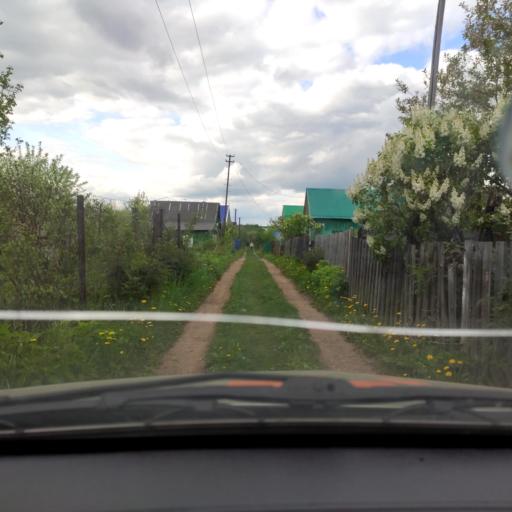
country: RU
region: Bashkortostan
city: Blagoveshchensk
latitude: 54.9413
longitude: 56.0851
